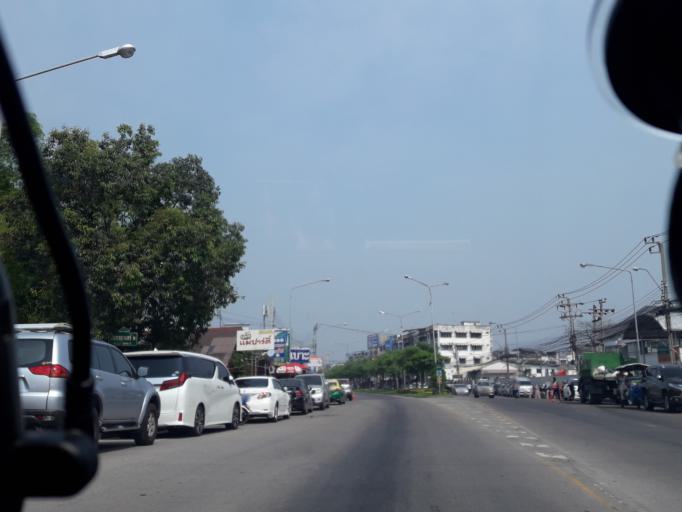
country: TH
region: Bangkok
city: Khan Na Yao
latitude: 13.8193
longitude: 100.6991
